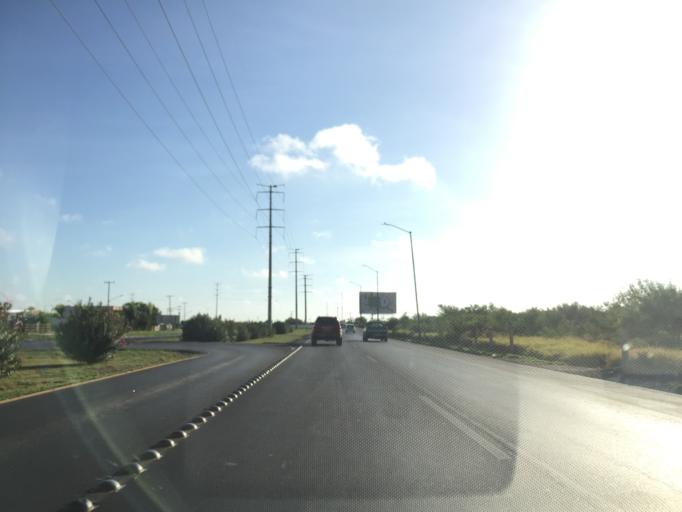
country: MX
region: Tamaulipas
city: Nuevo Laredo
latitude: 27.4336
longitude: -99.5012
